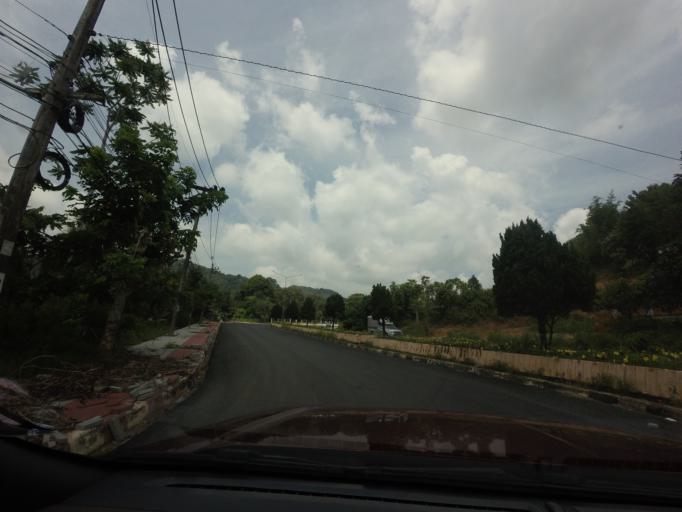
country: TH
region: Yala
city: Betong
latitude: 5.7521
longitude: 101.0419
